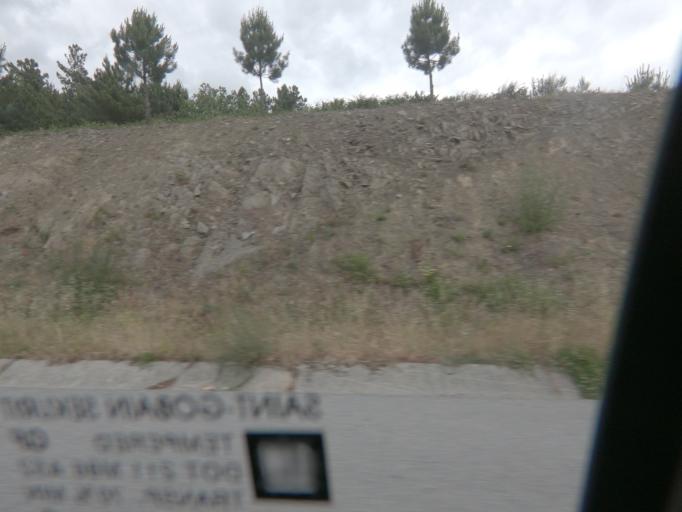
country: PT
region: Vila Real
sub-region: Sabrosa
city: Vilela
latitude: 41.2636
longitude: -7.6595
